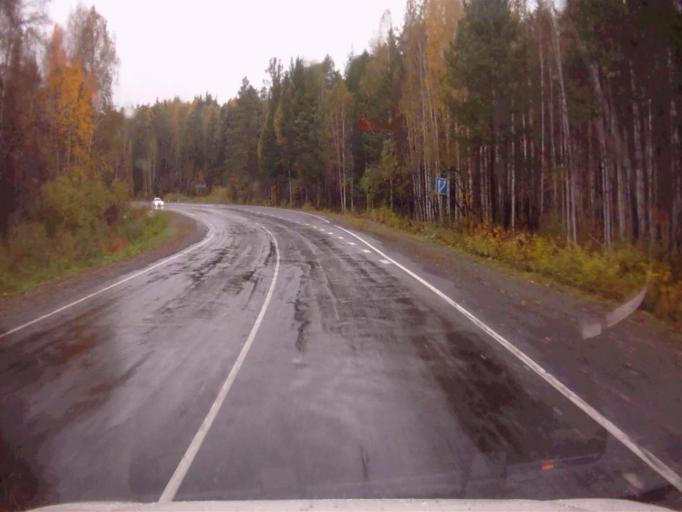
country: RU
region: Chelyabinsk
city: Verkhniy Ufaley
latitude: 55.9648
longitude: 60.3826
